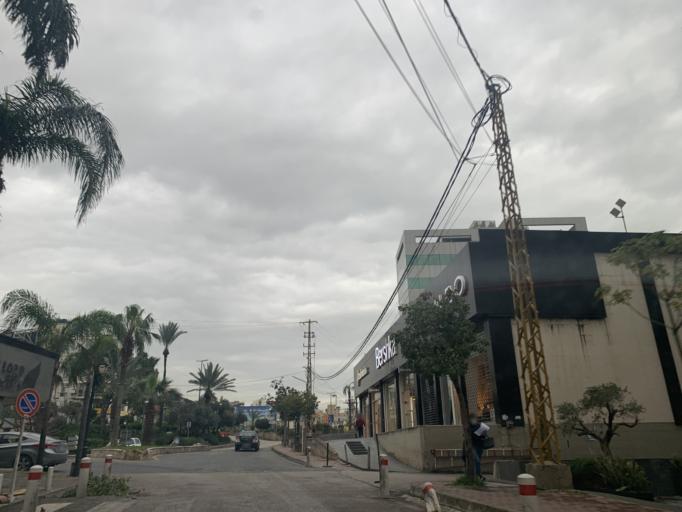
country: LB
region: Mont-Liban
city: Djounie
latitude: 33.9763
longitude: 35.6138
